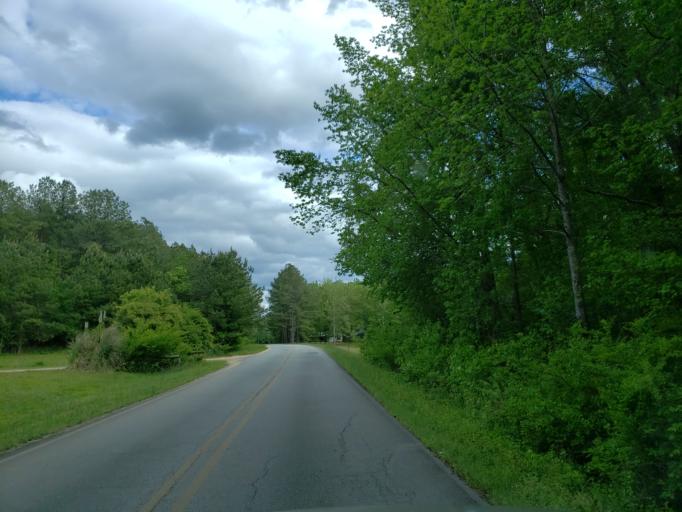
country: US
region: Georgia
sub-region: Haralson County
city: Tallapoosa
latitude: 33.7883
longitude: -85.3399
